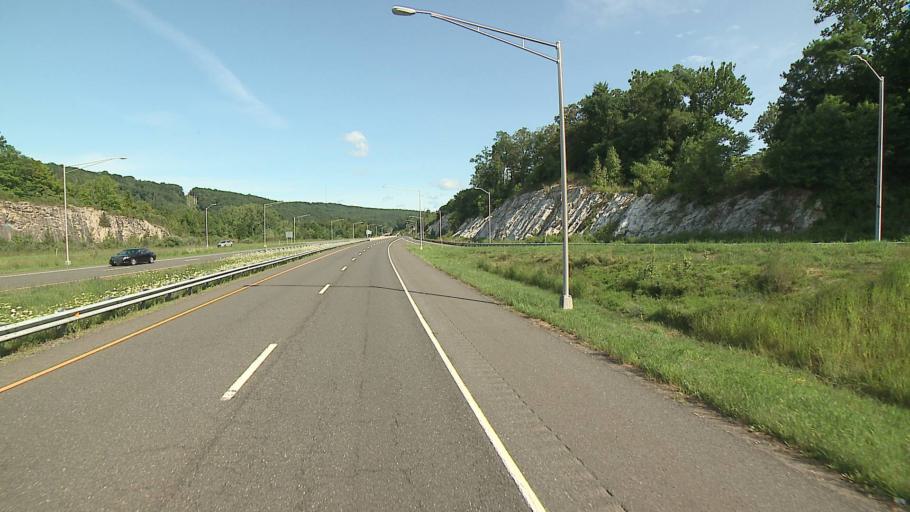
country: US
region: Connecticut
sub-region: Fairfield County
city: Danbury
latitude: 41.4738
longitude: -73.4094
